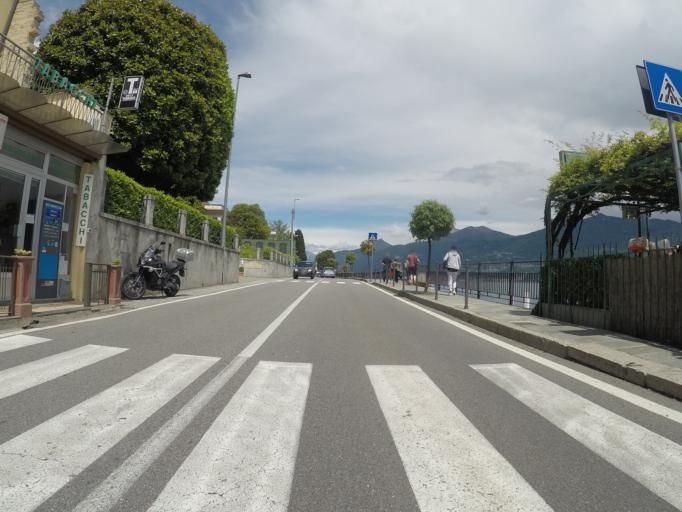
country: IT
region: Lombardy
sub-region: Provincia di Como
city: Cadenabbia
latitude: 45.9884
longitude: 9.2356
